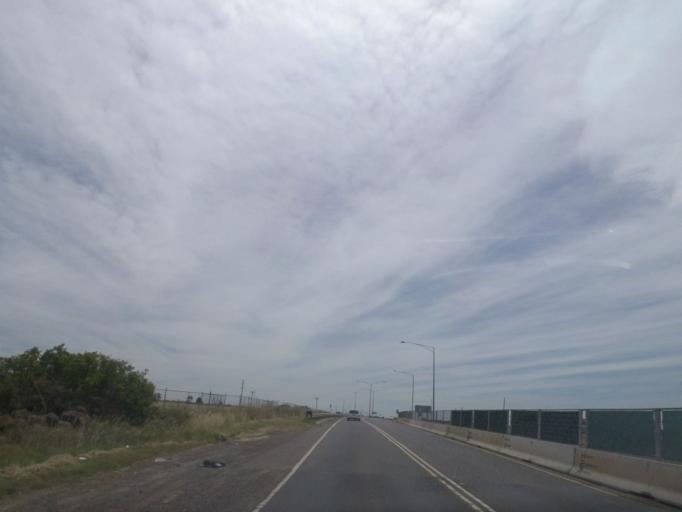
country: AU
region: Victoria
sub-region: Wyndham
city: Tarneit
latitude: -37.8215
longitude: 144.6933
